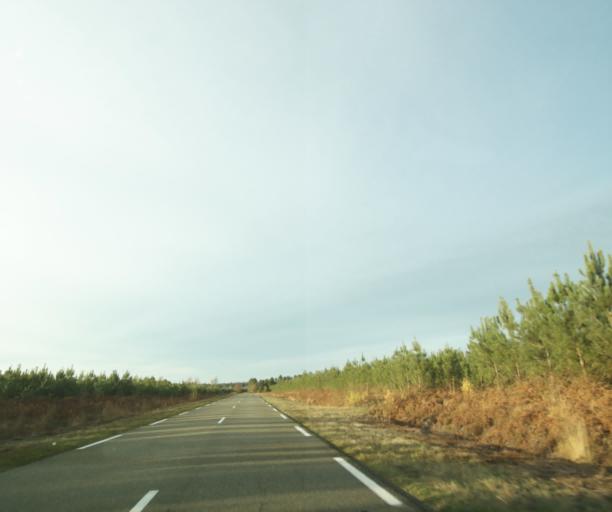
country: FR
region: Aquitaine
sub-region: Departement des Landes
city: Gabarret
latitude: 44.0828
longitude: -0.0729
